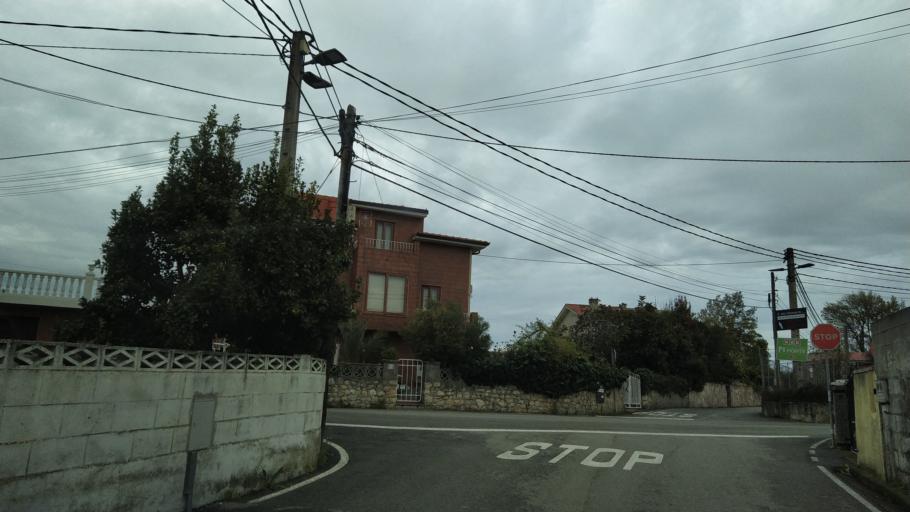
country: ES
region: Cantabria
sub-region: Provincia de Cantabria
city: Santander
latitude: 43.4710
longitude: -3.8250
